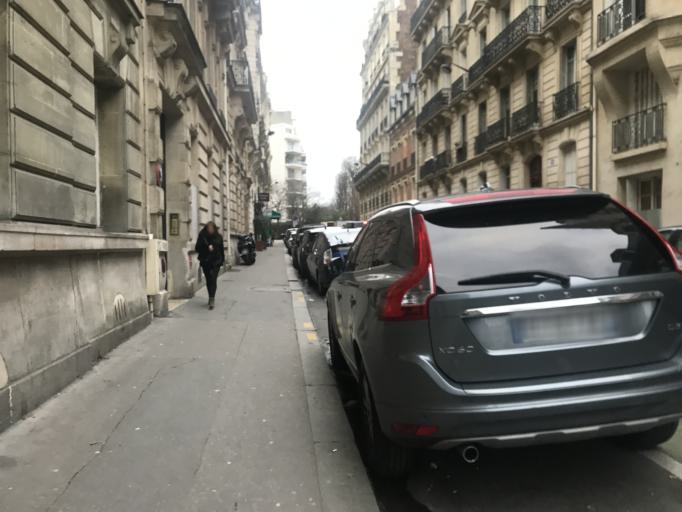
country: FR
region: Ile-de-France
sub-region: Departement des Hauts-de-Seine
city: Neuilly-sur-Seine
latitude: 48.8565
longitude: 2.2676
